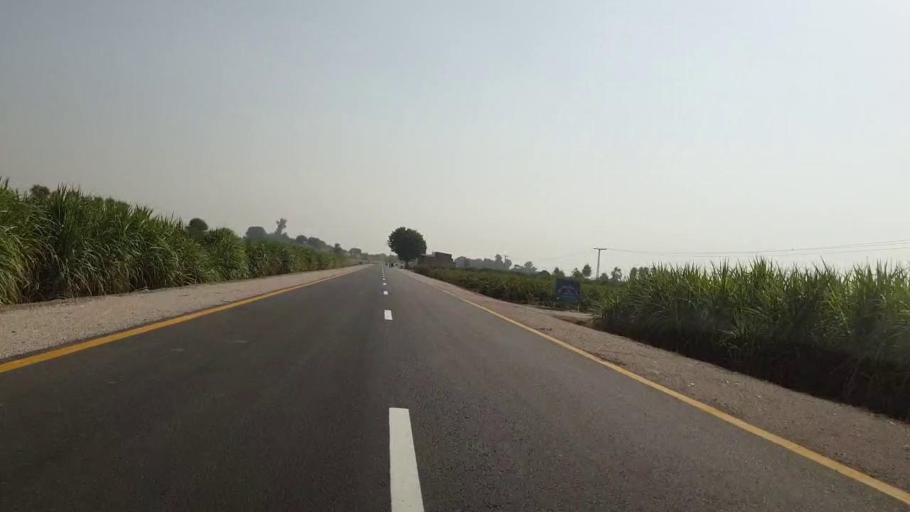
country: PK
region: Sindh
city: Bhan
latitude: 26.6064
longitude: 67.7791
